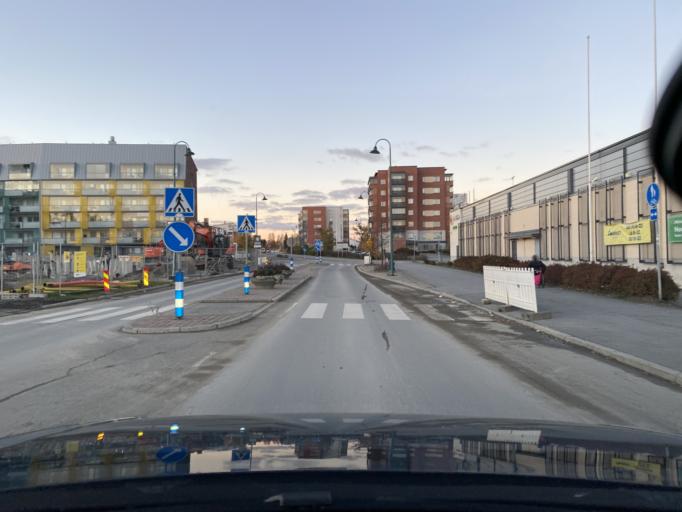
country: FI
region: Pirkanmaa
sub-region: Tampere
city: Lempaeaelae
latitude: 61.3133
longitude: 23.7588
